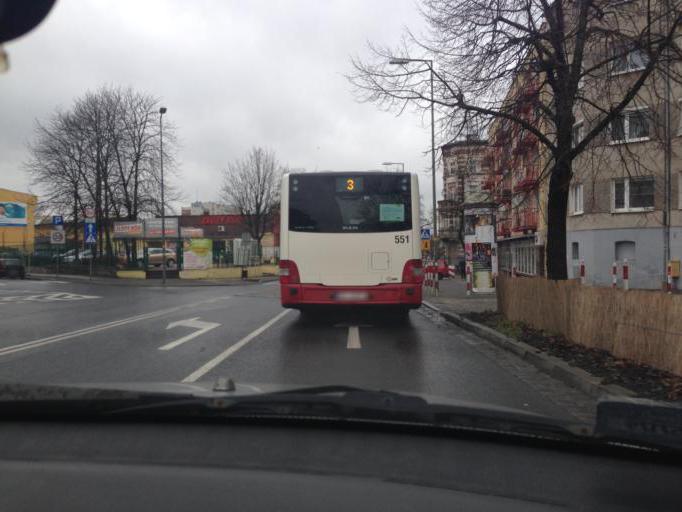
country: PL
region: Opole Voivodeship
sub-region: Powiat opolski
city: Opole
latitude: 50.6711
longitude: 17.9235
